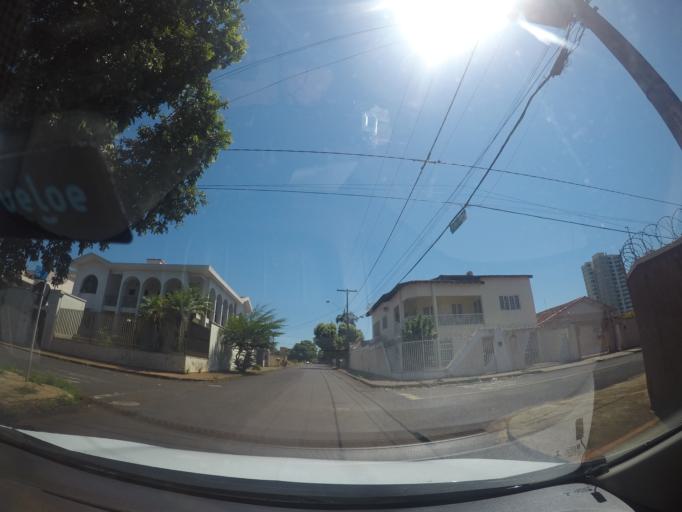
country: BR
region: Goias
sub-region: Itumbiara
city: Itumbiara
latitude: -18.4122
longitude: -49.2039
